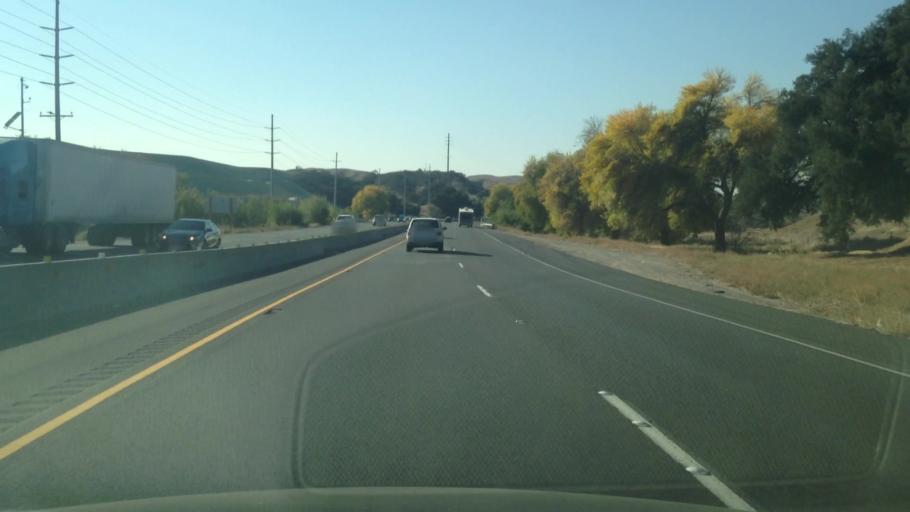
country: US
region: California
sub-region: Riverside County
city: Beaumont
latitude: 33.9328
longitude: -117.0251
